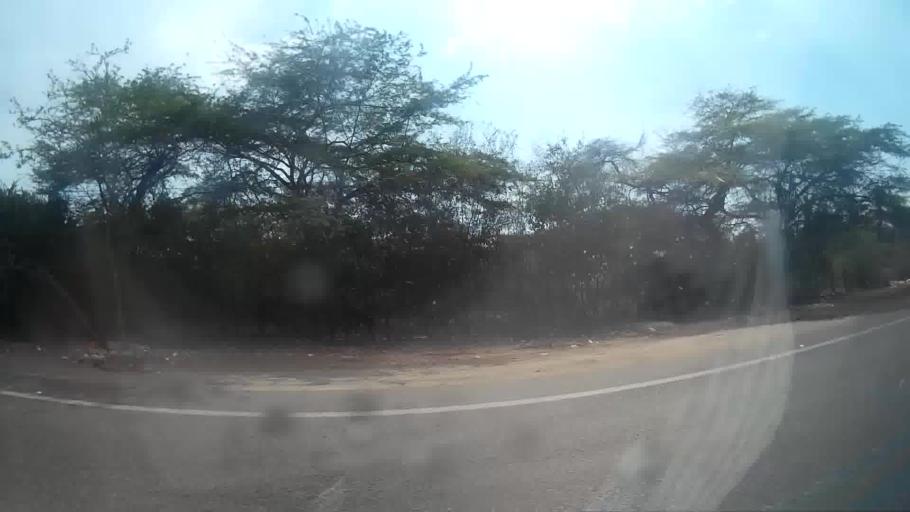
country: CO
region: Magdalena
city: Cienaga
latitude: 11.1169
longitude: -74.2244
